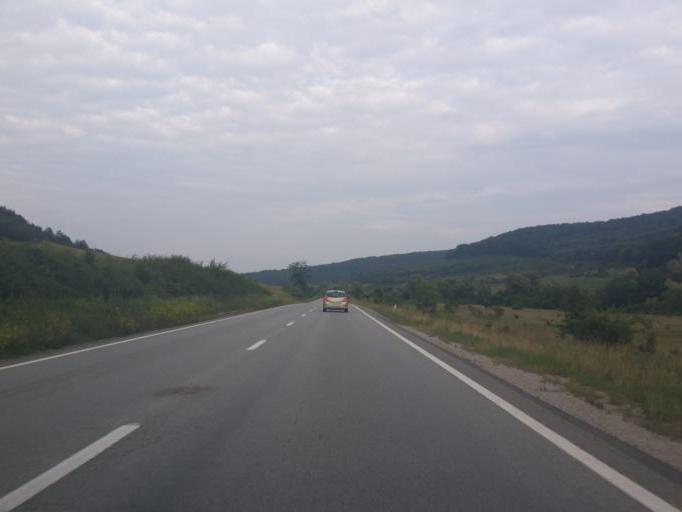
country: RO
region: Salaj
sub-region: Comuna Zimbor
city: Zimbor
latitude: 46.9723
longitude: 23.2607
